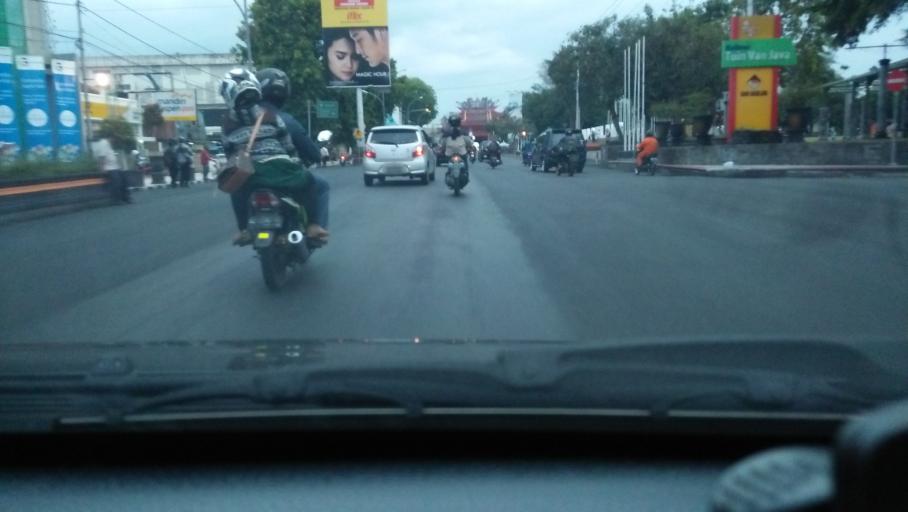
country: ID
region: Central Java
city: Magelang
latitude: -7.4762
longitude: 110.2188
